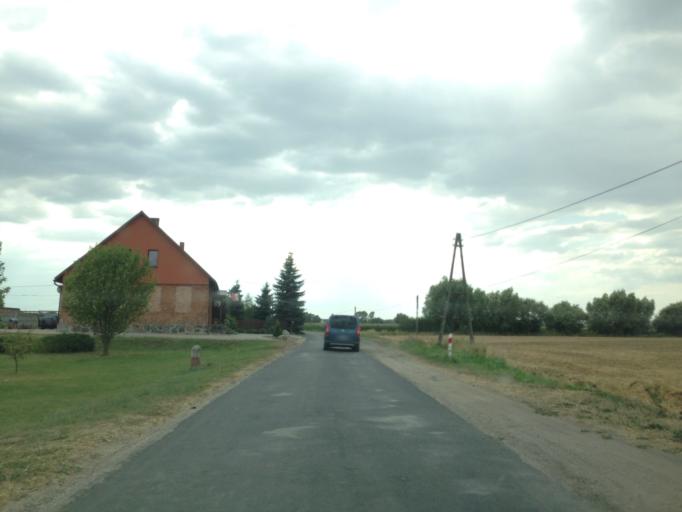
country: PL
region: Kujawsko-Pomorskie
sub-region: Powiat chelminski
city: Chelmno
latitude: 53.3569
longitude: 18.3703
